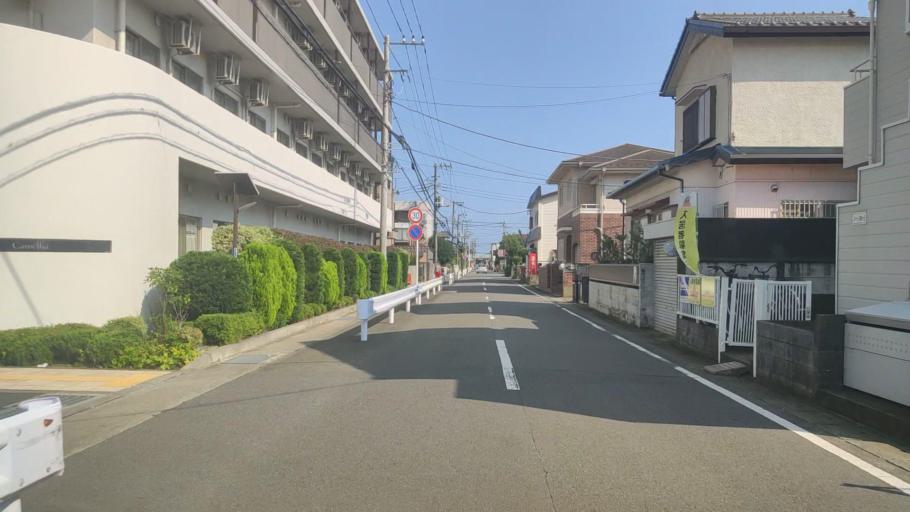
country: JP
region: Kanagawa
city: Hiratsuka
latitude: 35.3302
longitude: 139.3249
